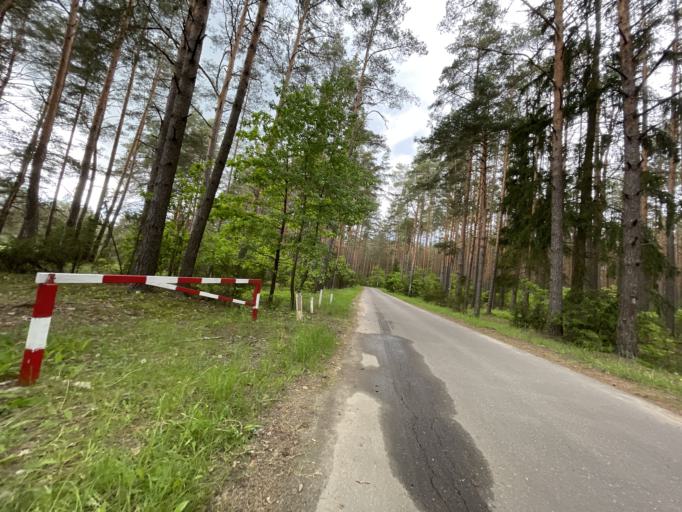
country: BY
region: Minsk
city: Stowbtsy
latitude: 53.4270
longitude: 26.8125
